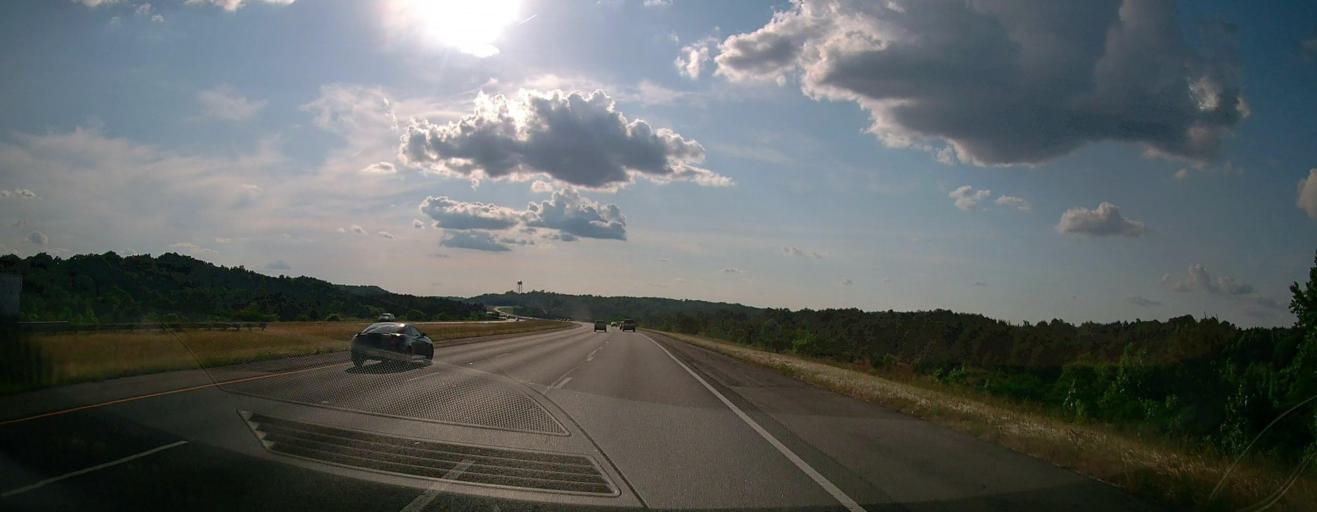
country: US
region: Alabama
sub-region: Jefferson County
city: Graysville
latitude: 33.6628
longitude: -87.0234
